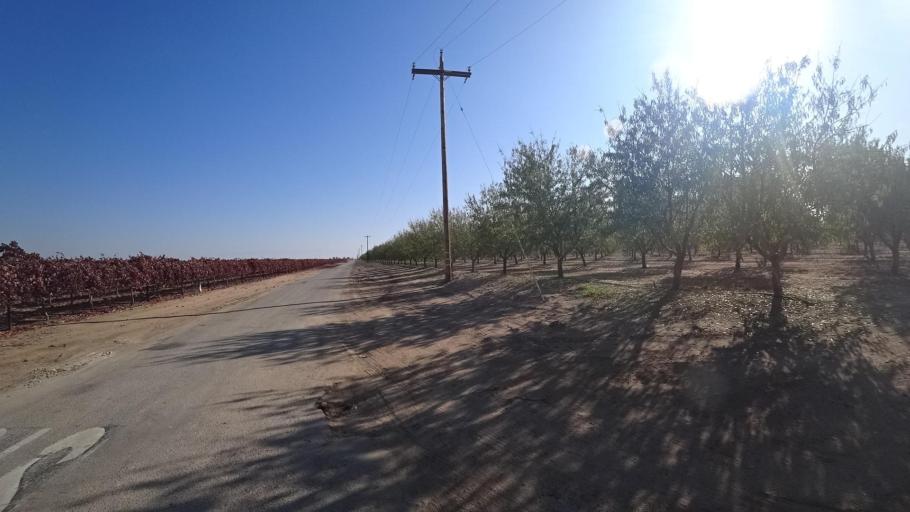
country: US
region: California
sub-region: Kern County
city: Delano
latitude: 35.7397
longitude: -119.2230
